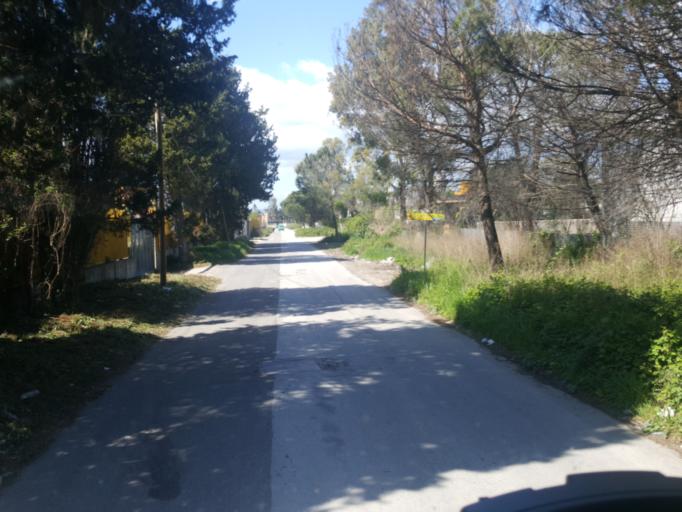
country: IT
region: Campania
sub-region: Provincia di Napoli
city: Torretta-Scalzapecora
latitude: 40.9324
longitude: 14.1065
